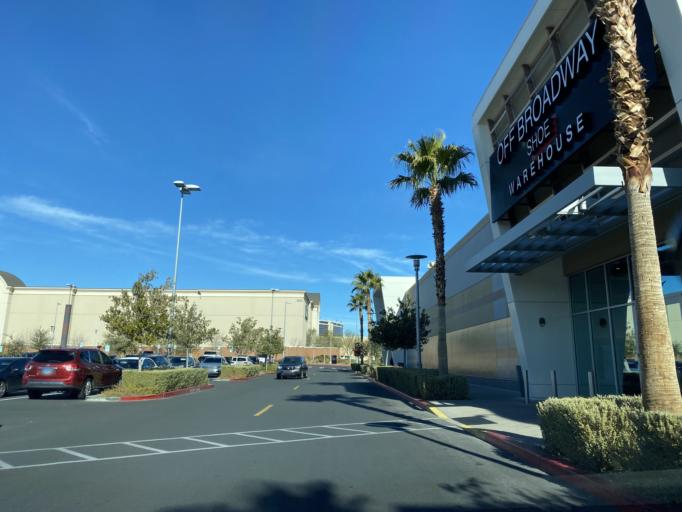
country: US
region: Nevada
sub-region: Clark County
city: Summerlin South
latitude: 36.1464
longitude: -115.3327
